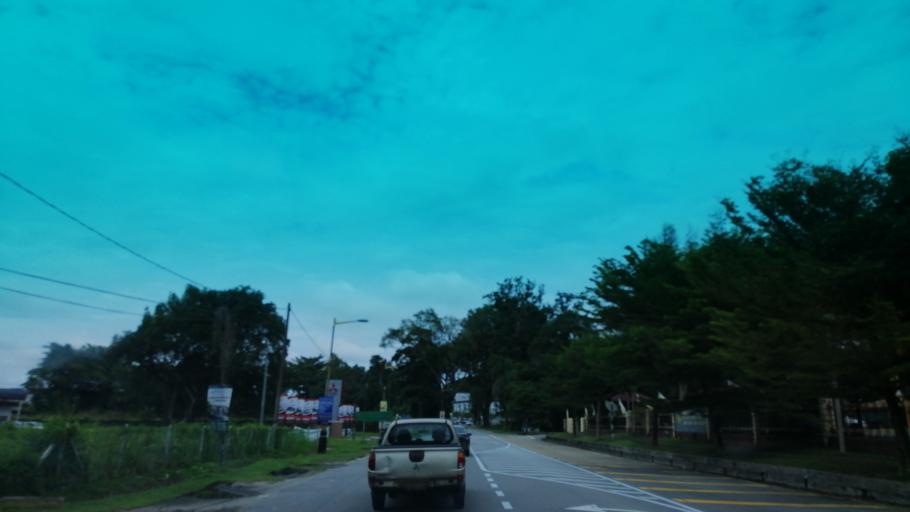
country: MY
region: Perak
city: Taiping
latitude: 4.8573
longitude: 100.7392
